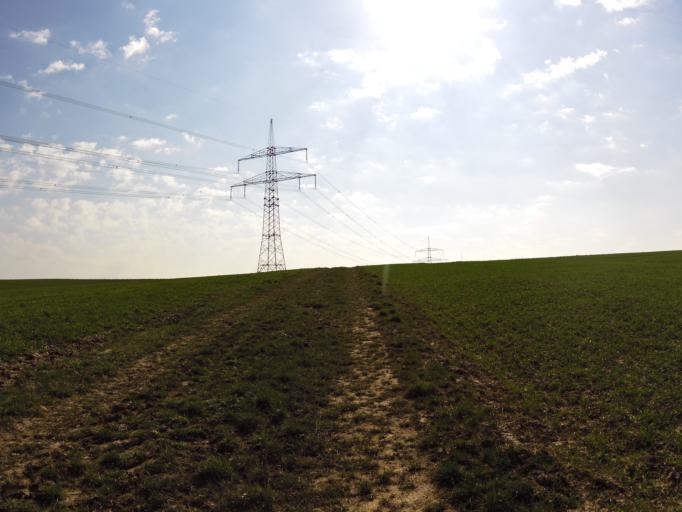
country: DE
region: Bavaria
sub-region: Regierungsbezirk Unterfranken
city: Rottendorf
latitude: 49.8033
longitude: 10.0676
